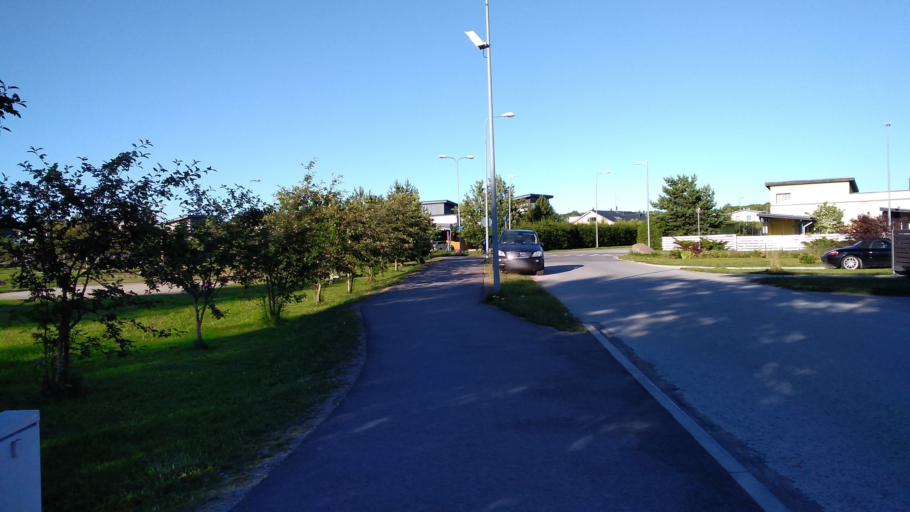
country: EE
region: Harju
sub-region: Viimsi vald
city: Viimsi
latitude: 59.5004
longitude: 24.8570
